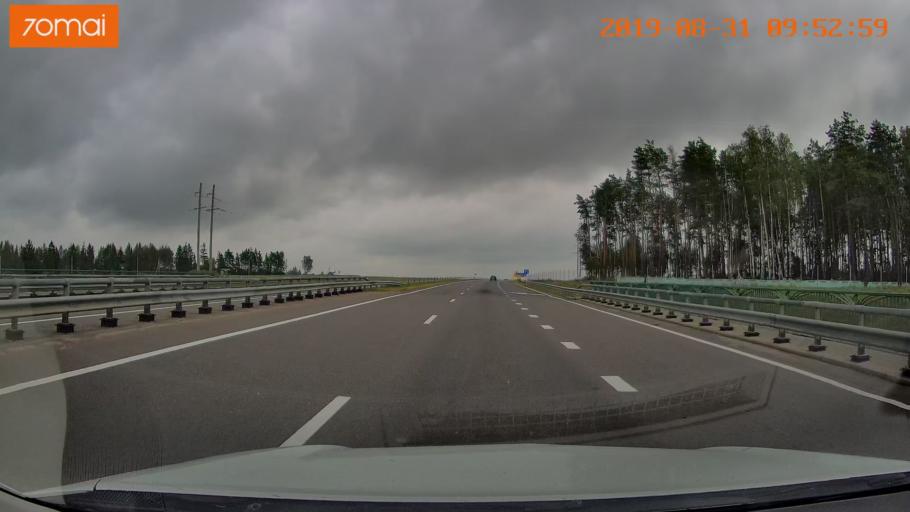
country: BY
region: Mogilev
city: Byalynichy
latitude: 53.9829
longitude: 29.7928
